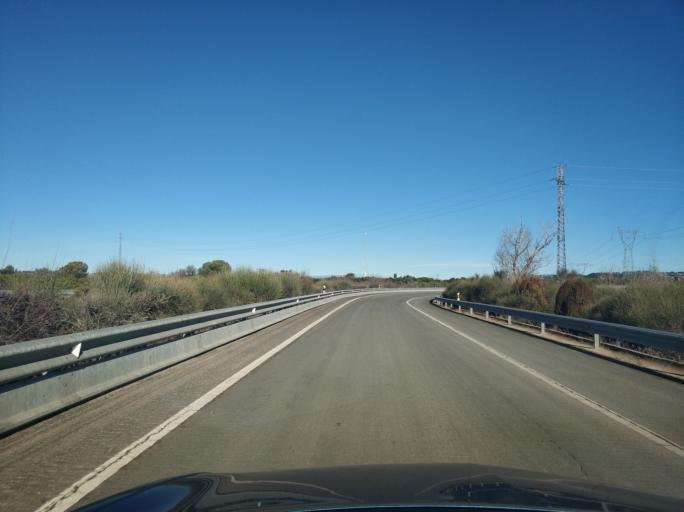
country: ES
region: Castille and Leon
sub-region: Provincia de Valladolid
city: Tordesillas
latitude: 41.5108
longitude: -5.0155
